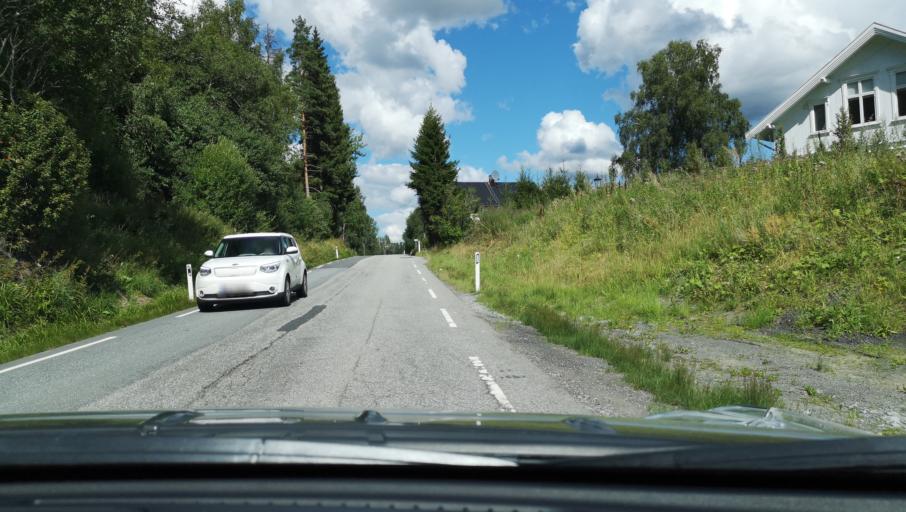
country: NO
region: Ostfold
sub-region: Hobol
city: Elvestad
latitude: 59.6355
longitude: 10.9620
